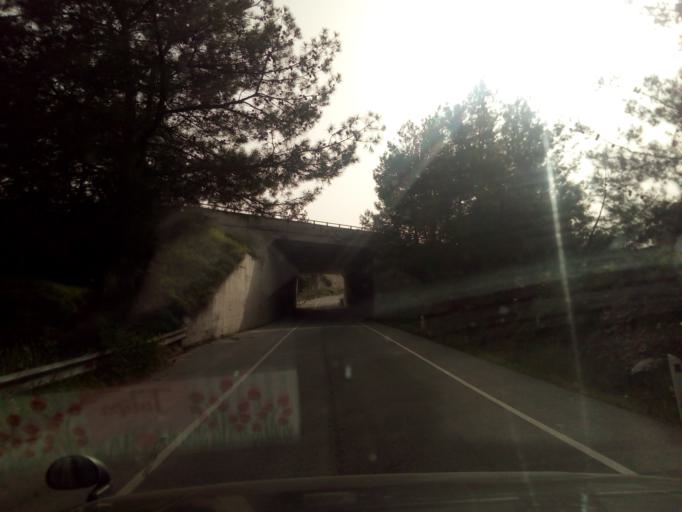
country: CY
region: Lefkosia
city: Lympia
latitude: 34.9942
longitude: 33.4852
